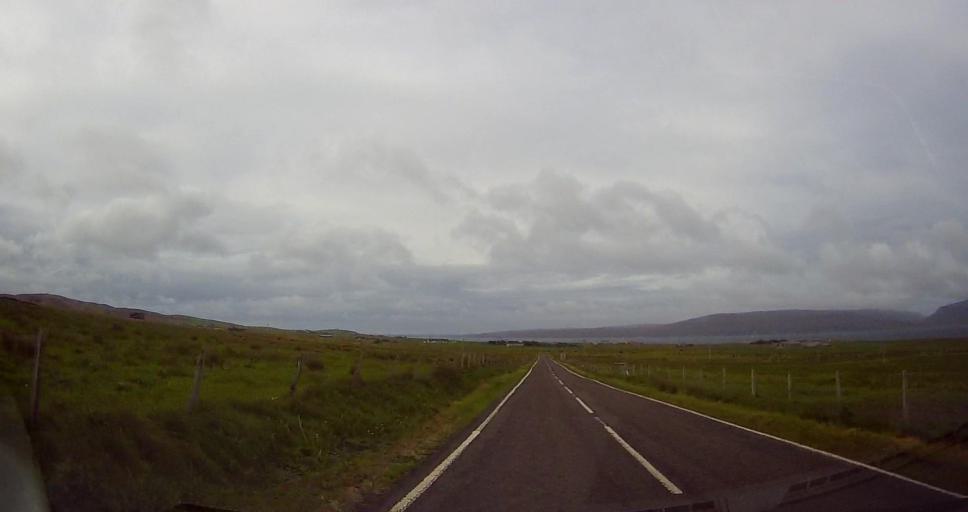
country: GB
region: Scotland
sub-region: Orkney Islands
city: Stromness
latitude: 58.9459
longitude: -3.2144
